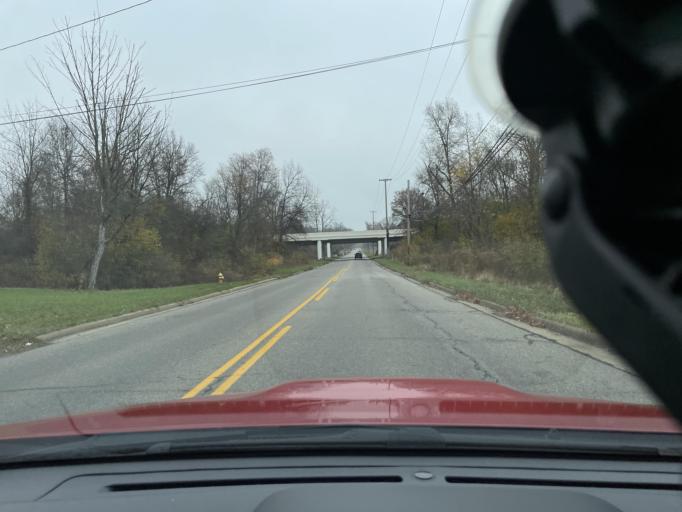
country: US
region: Ohio
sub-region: Mahoning County
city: Austintown
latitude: 41.1057
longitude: -80.7570
